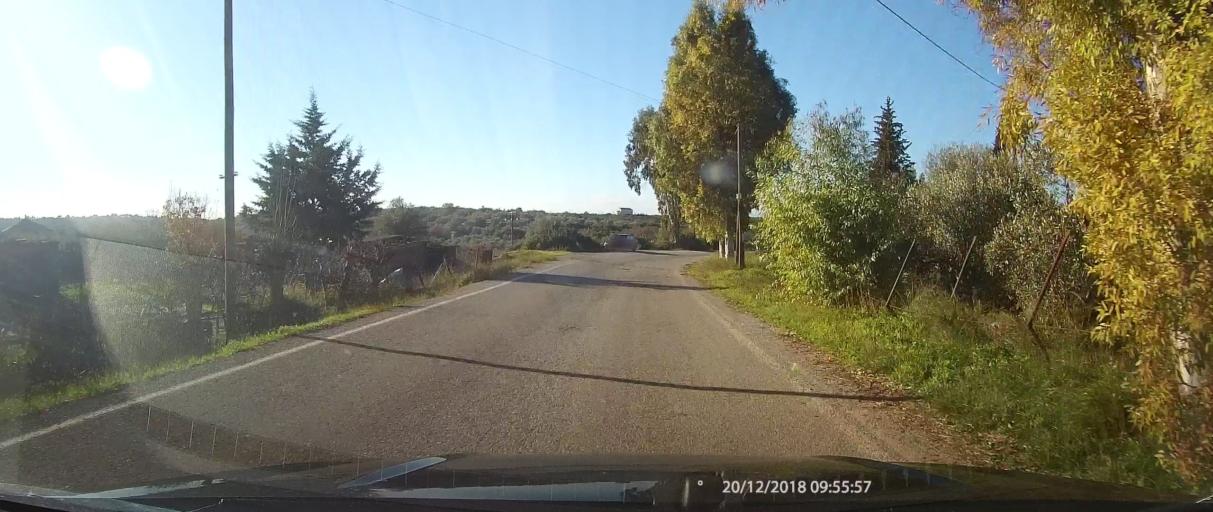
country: GR
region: Peloponnese
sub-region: Nomos Lakonias
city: Yerakion
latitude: 37.0234
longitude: 22.6180
